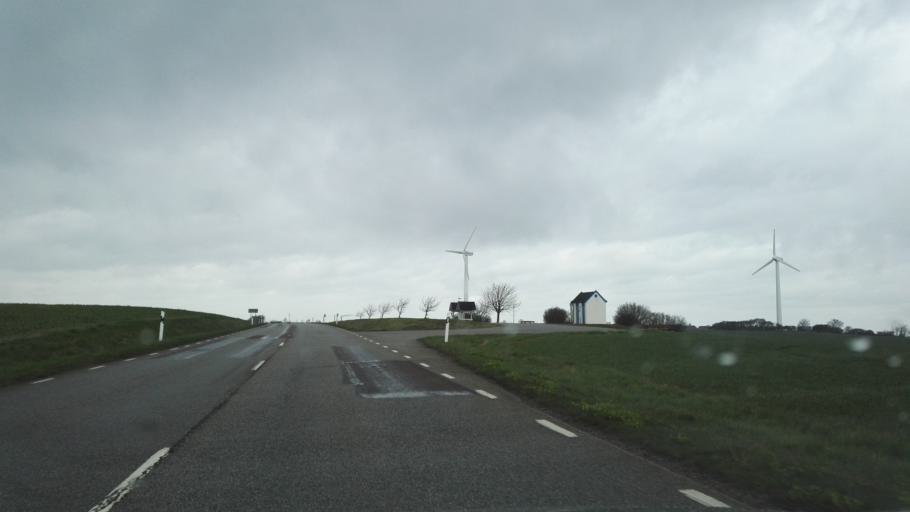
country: SE
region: Skane
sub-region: Simrishamns Kommun
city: Simrishamn
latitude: 55.5337
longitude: 14.3402
